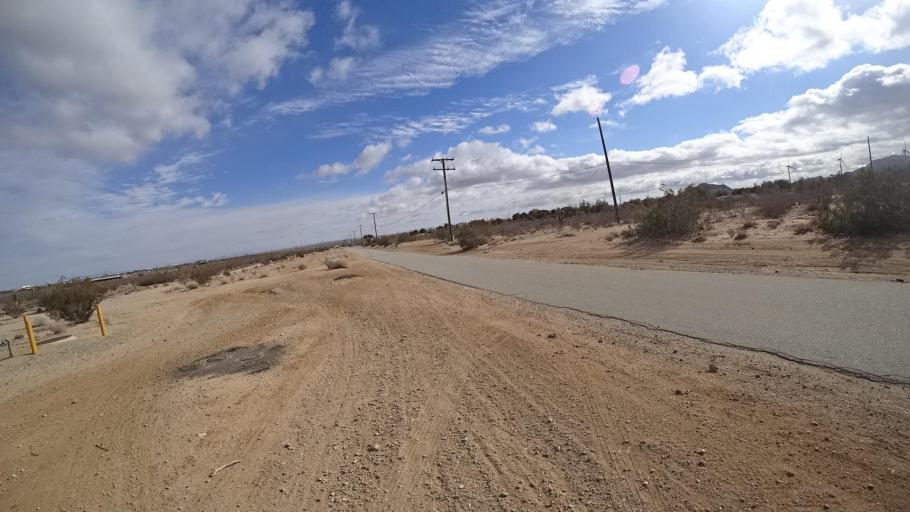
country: US
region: California
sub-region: Kern County
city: Mojave
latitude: 35.0316
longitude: -118.1948
